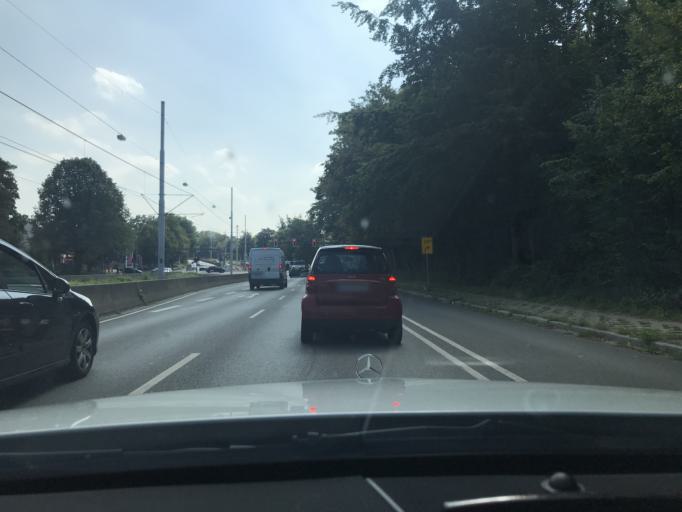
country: DE
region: North Rhine-Westphalia
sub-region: Regierungsbezirk Arnsberg
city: Bochum
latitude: 51.4585
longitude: 7.2371
